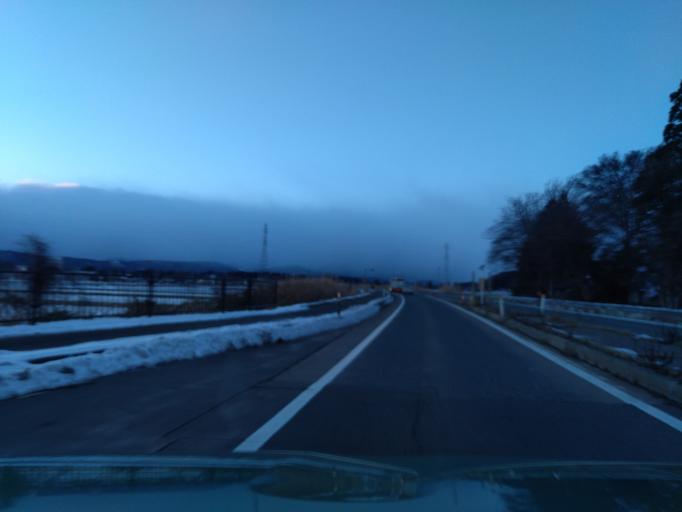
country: JP
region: Iwate
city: Shizukuishi
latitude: 39.6996
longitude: 140.9763
